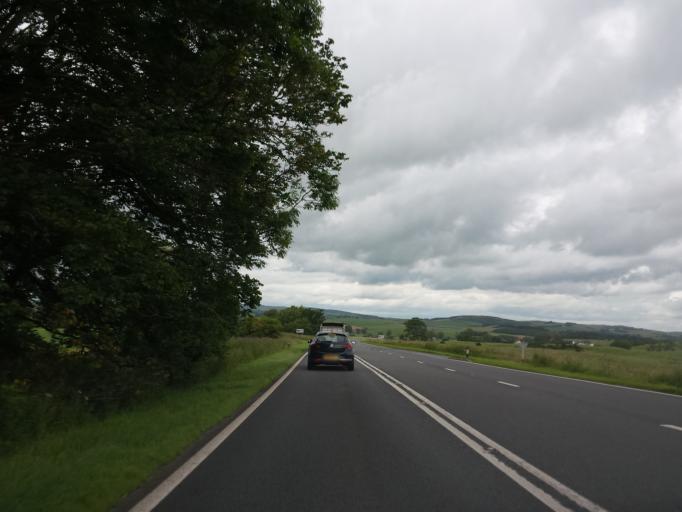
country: GB
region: Scotland
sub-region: Dumfries and Galloway
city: Castle Douglas
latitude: 54.9673
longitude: -3.9036
